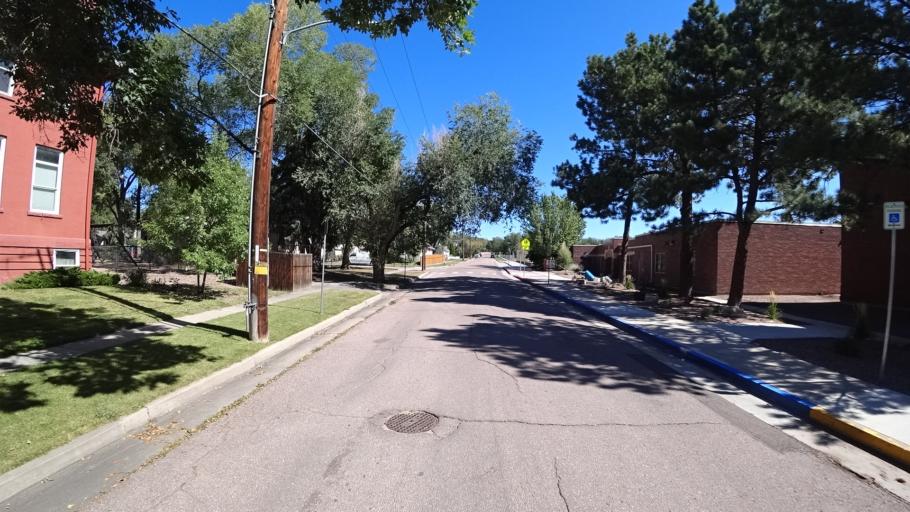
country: US
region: Colorado
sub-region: El Paso County
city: Colorado Springs
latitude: 38.8437
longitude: -104.8542
